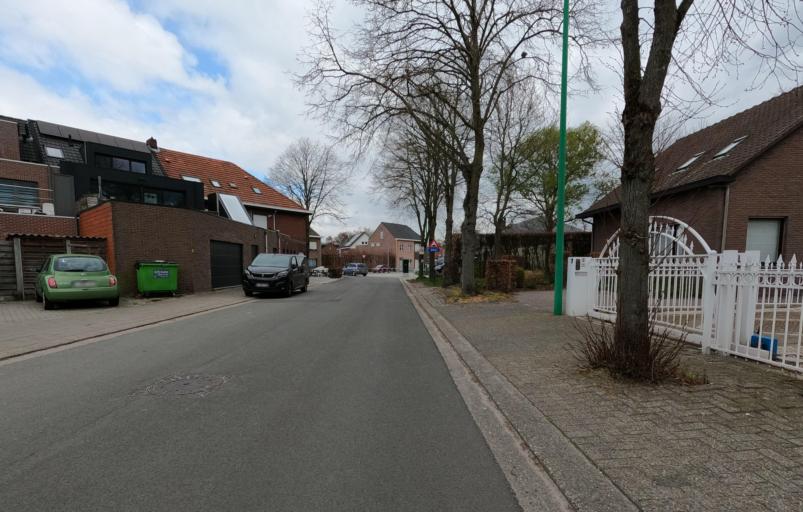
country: BE
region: Flanders
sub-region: Provincie Antwerpen
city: Essen
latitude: 51.4682
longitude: 4.5012
